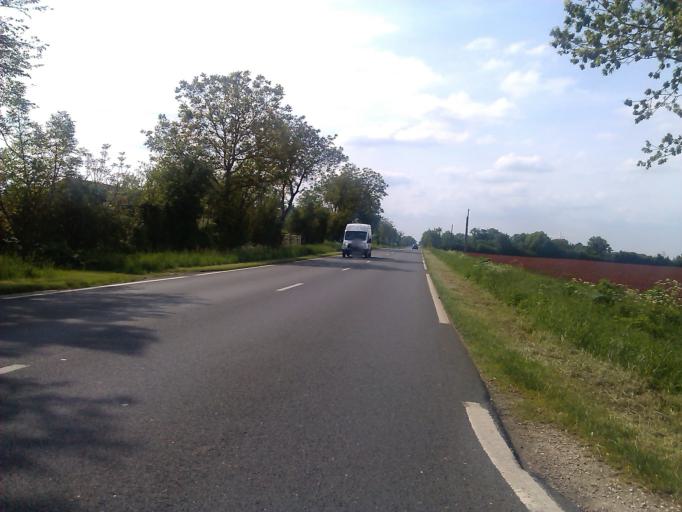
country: FR
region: Centre
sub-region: Departement de l'Indre
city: La Chatre
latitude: 46.5684
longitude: 2.0332
